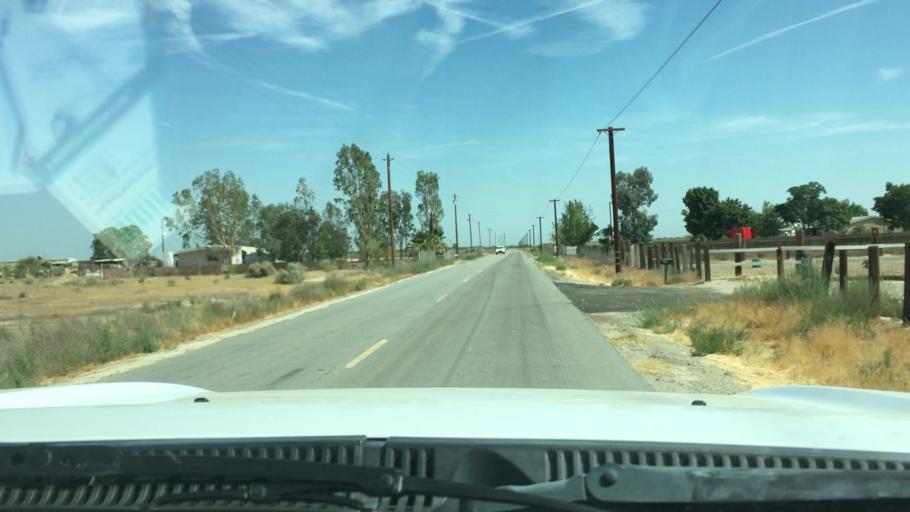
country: US
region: California
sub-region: Kern County
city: Buttonwillow
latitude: 35.4286
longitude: -119.3762
